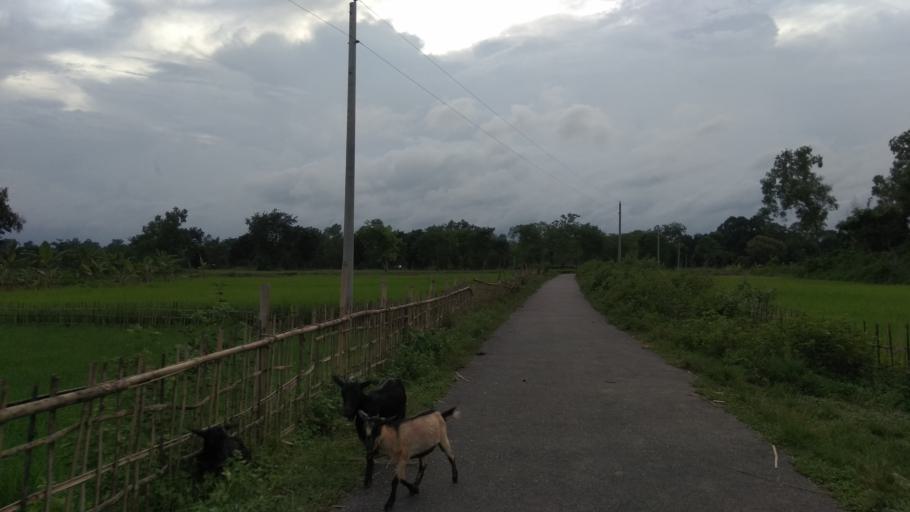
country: IN
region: Tripura
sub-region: Dhalai
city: Kamalpur
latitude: 24.1759
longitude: 91.8807
